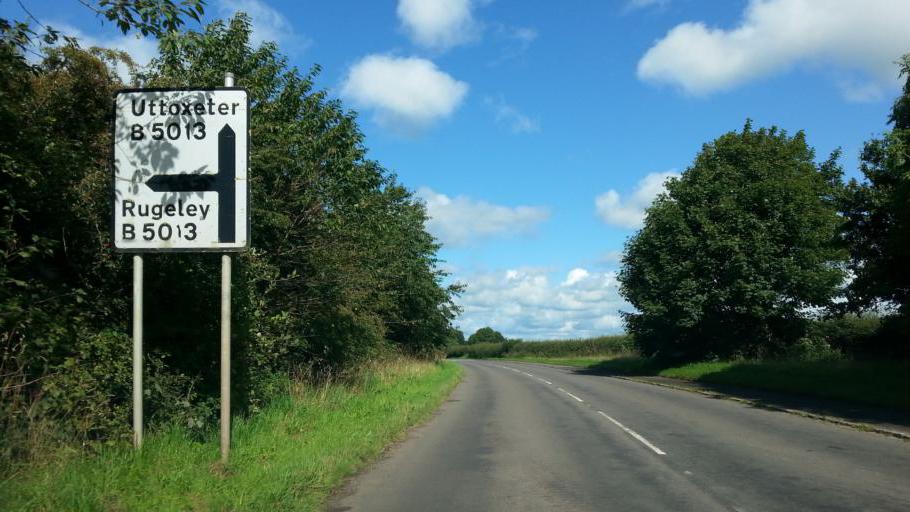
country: GB
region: England
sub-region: Staffordshire
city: Rugeley
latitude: 52.8241
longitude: -1.8938
